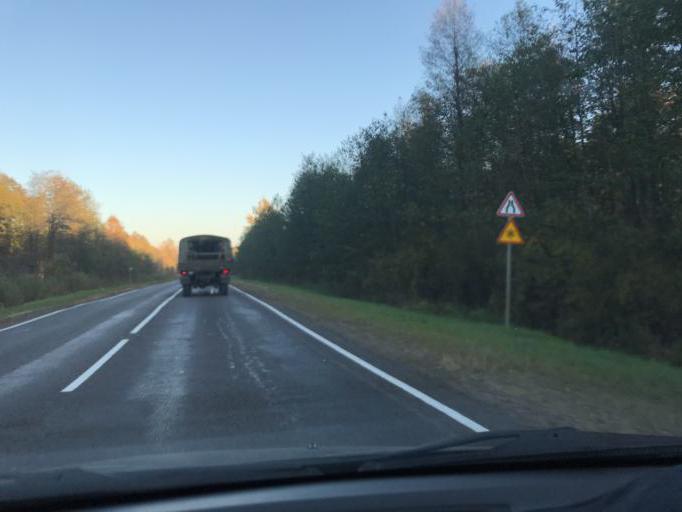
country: BY
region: Minsk
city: Staryya Darohi
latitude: 53.0431
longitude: 28.1426
